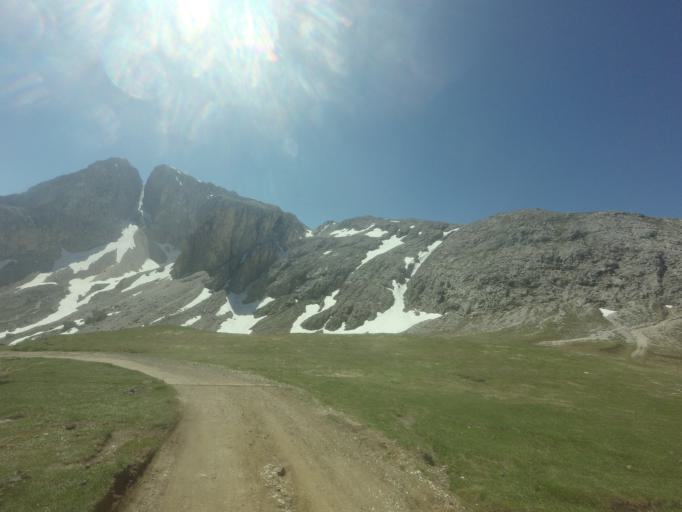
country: IT
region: Trentino-Alto Adige
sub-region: Provincia di Trento
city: Mazzin
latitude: 46.4964
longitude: 11.6342
